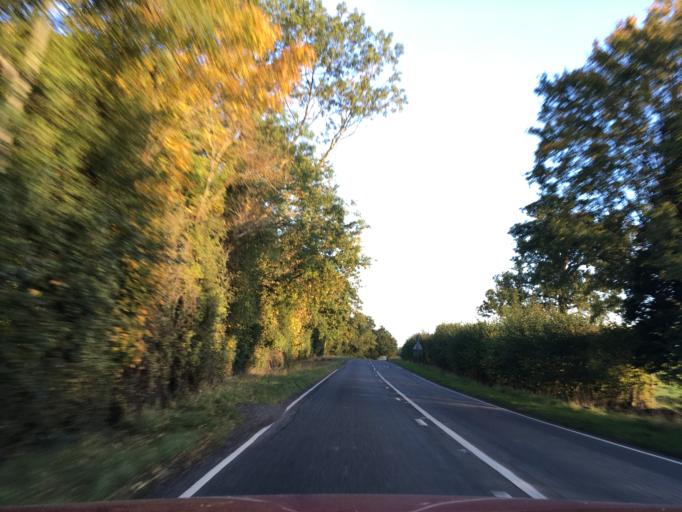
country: GB
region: England
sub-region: Herefordshire
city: Donnington
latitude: 52.0217
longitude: -2.3303
